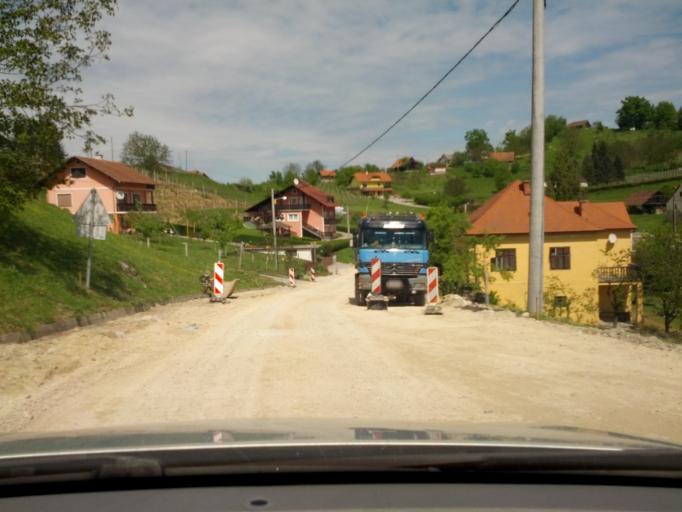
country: SI
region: Bistrica ob Sotli
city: Bistrica ob Sotli
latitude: 46.0959
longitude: 15.6336
